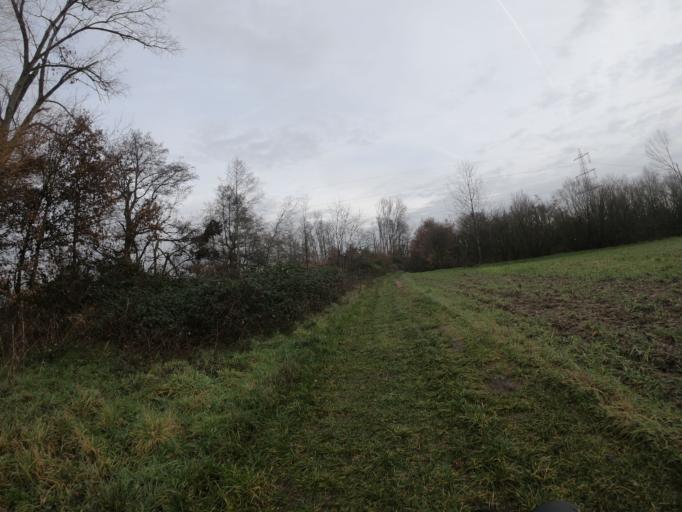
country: DE
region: Hesse
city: Morfelden-Walldorf
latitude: 49.9753
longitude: 8.5826
